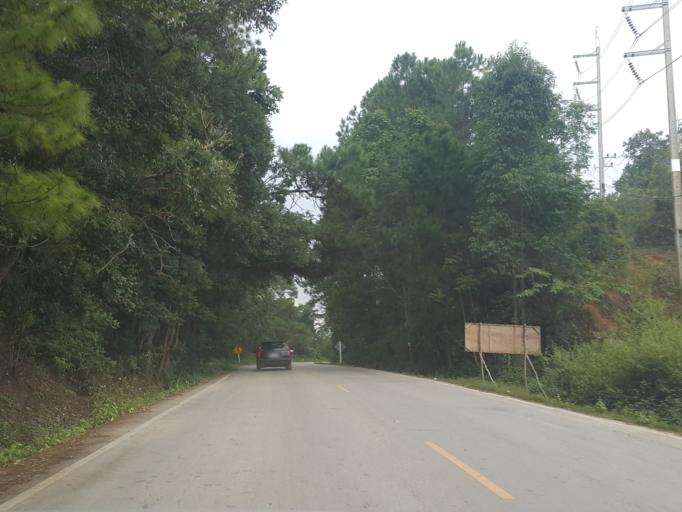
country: TH
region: Mae Hong Son
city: Mae Hi
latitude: 19.2719
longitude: 98.5576
